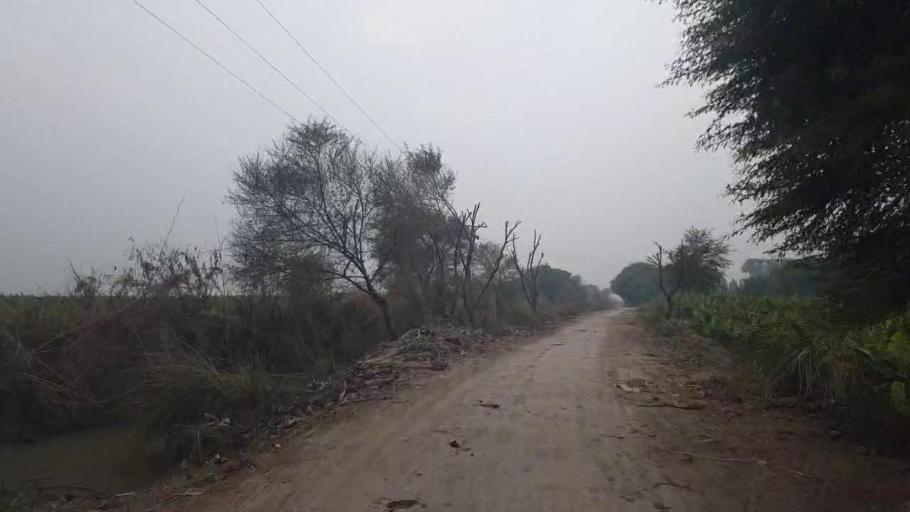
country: PK
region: Sindh
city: Tando Adam
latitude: 25.7455
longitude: 68.7070
